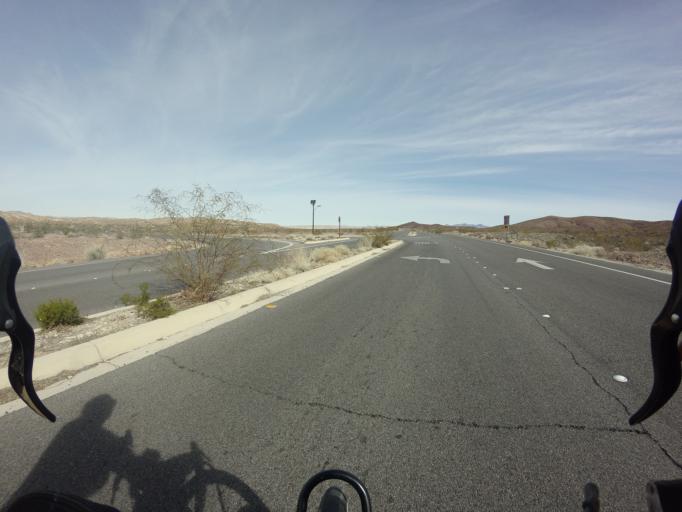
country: US
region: Nevada
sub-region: Clark County
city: Henderson
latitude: 36.1428
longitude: -114.8890
